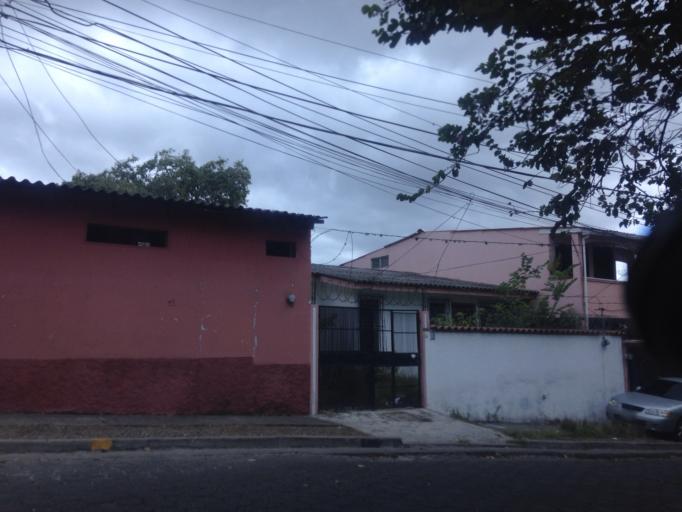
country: HN
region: Francisco Morazan
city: Tegucigalpa
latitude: 14.0561
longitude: -87.2369
